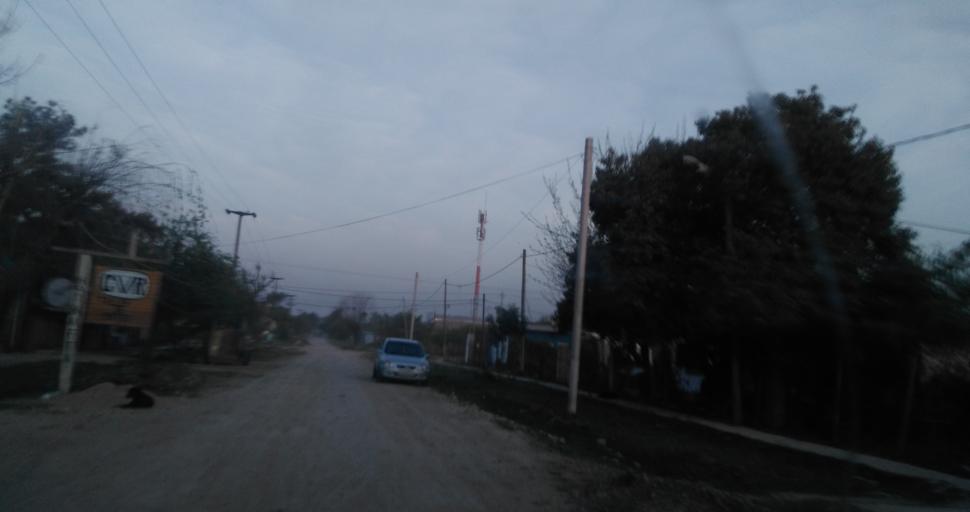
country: AR
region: Chaco
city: Resistencia
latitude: -27.4706
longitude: -59.0146
